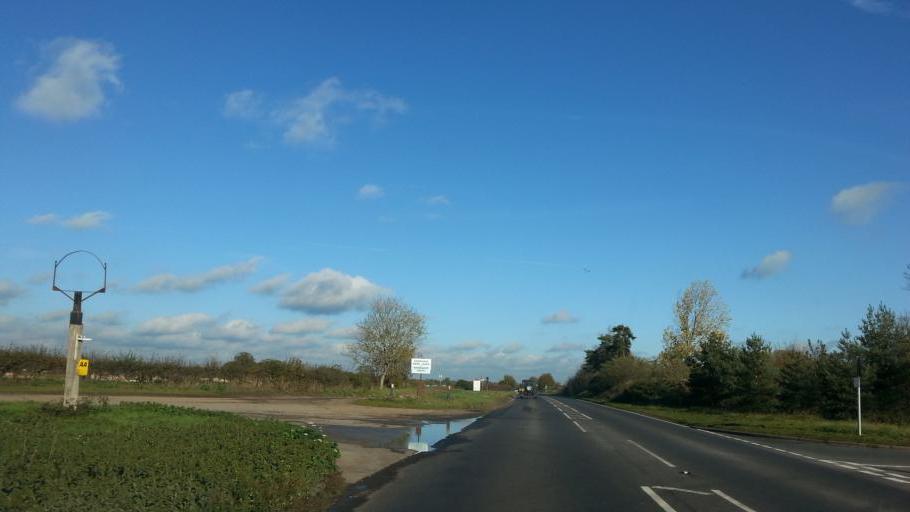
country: GB
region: England
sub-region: Suffolk
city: Bungay
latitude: 52.4417
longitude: 1.3972
